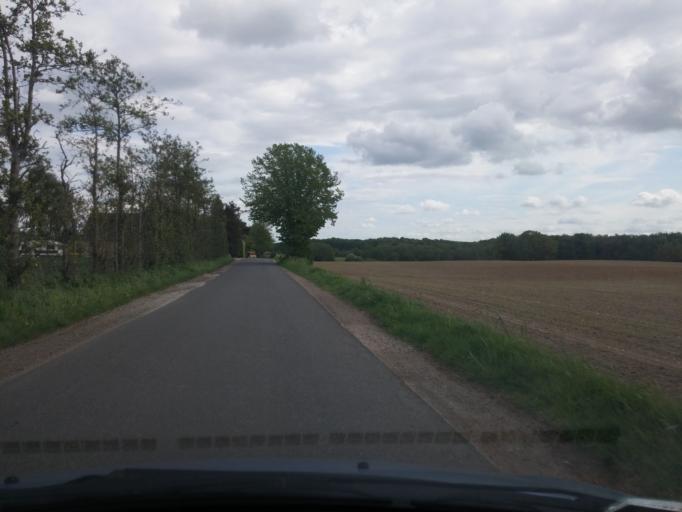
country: DK
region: South Denmark
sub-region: Nyborg Kommune
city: Ullerslev
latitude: 55.3838
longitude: 10.6404
